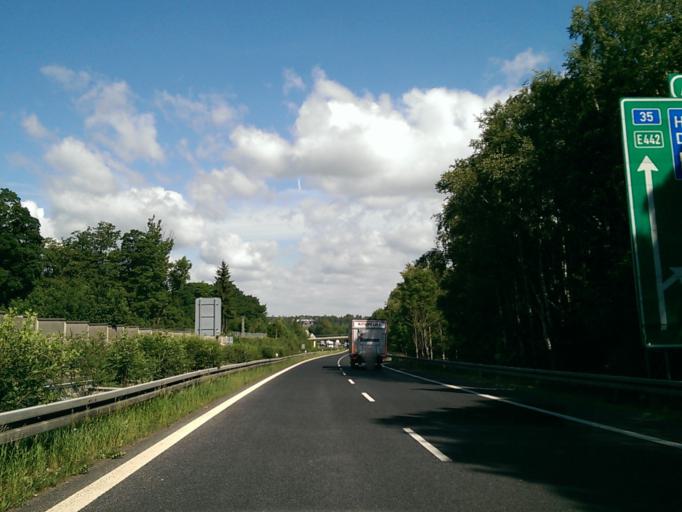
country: CZ
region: Liberecky
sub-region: Okres Liberec
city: Liberec
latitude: 50.7252
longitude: 15.0607
